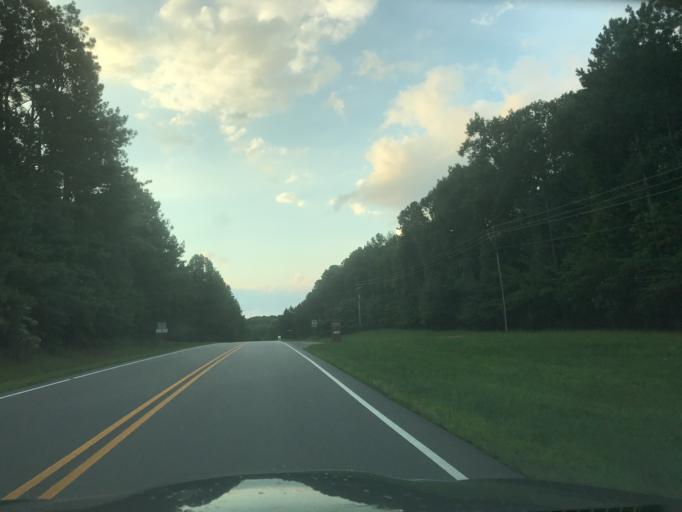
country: US
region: North Carolina
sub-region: Wake County
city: Wake Forest
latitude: 35.9259
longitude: -78.6046
